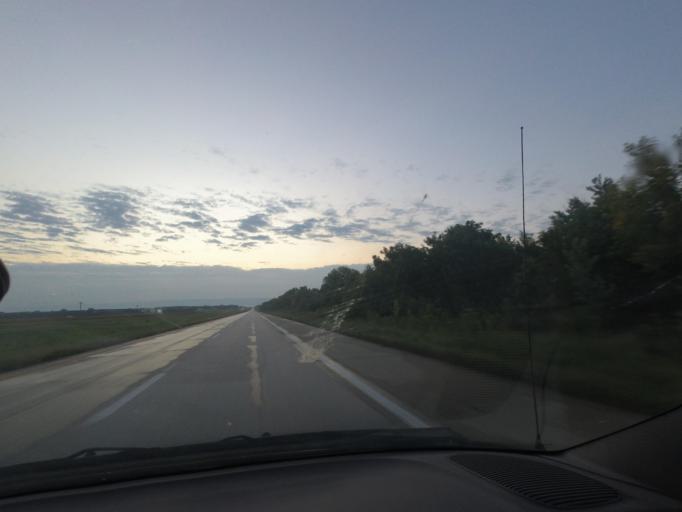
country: US
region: Missouri
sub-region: Macon County
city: Macon
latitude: 39.7599
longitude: -92.6878
